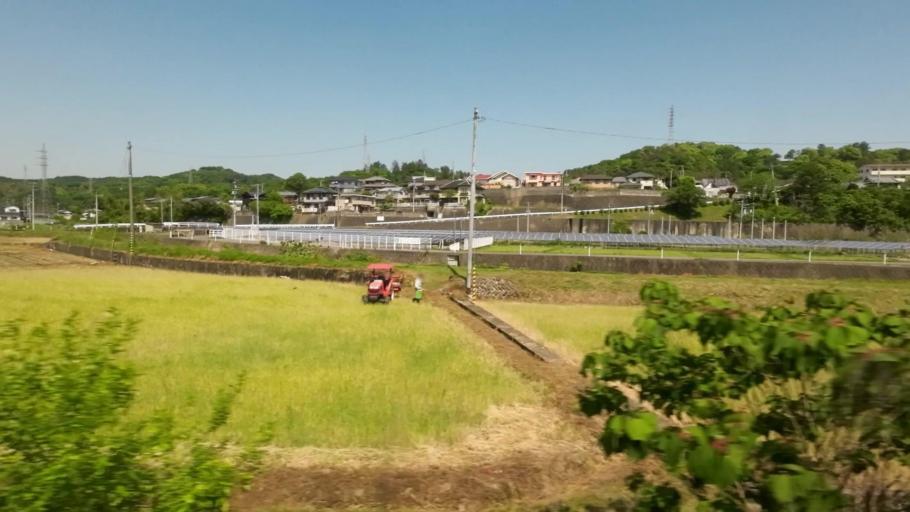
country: JP
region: Ehime
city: Niihama
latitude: 33.9303
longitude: 133.2699
